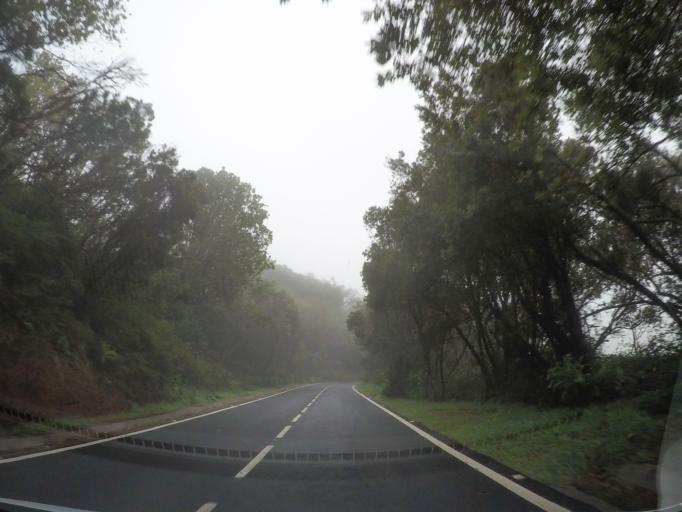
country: ES
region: Canary Islands
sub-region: Provincia de Santa Cruz de Tenerife
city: Vallehermosa
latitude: 28.1227
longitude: -17.2517
